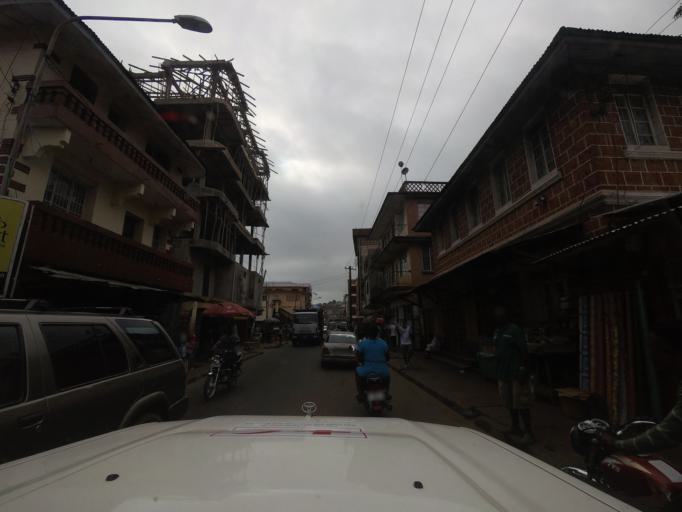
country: SL
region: Western Area
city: Freetown
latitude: 8.4834
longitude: -13.2424
